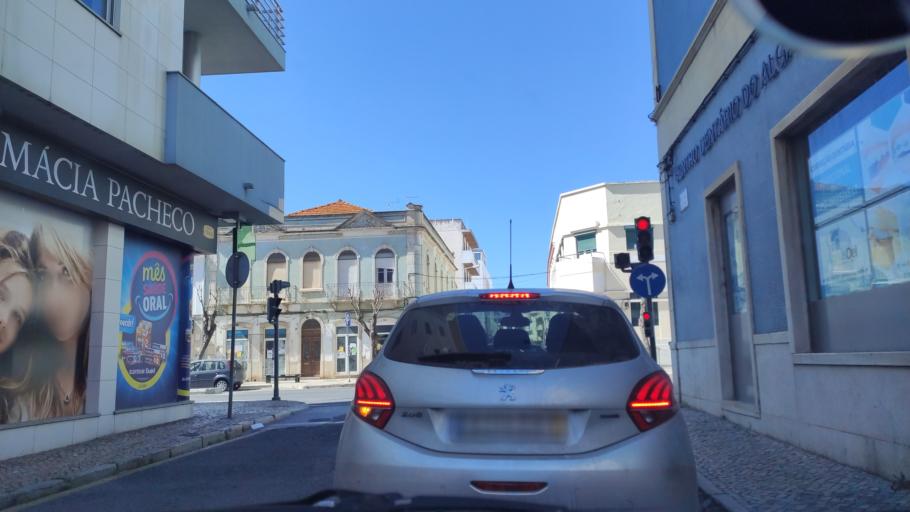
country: PT
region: Faro
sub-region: Olhao
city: Olhao
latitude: 37.0327
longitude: -7.8372
